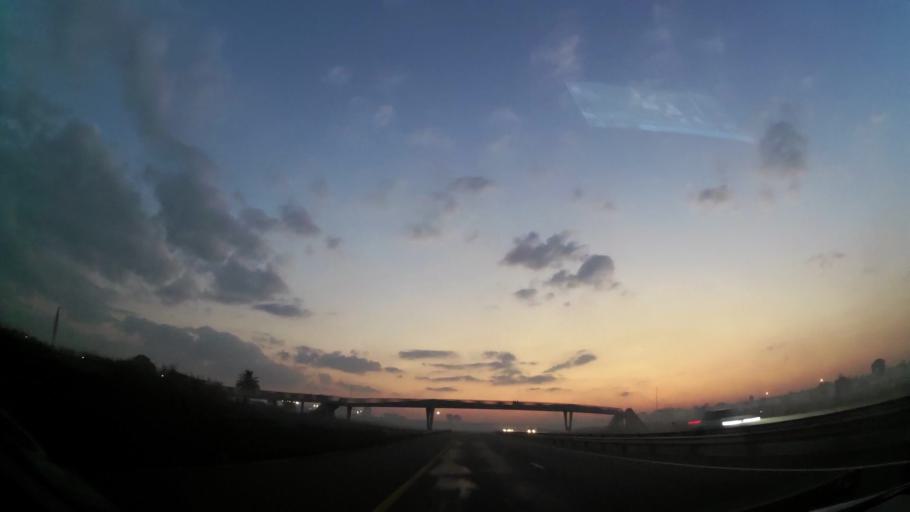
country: ZA
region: Gauteng
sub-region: Ekurhuleni Metropolitan Municipality
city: Springs
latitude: -26.2759
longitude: 28.3823
